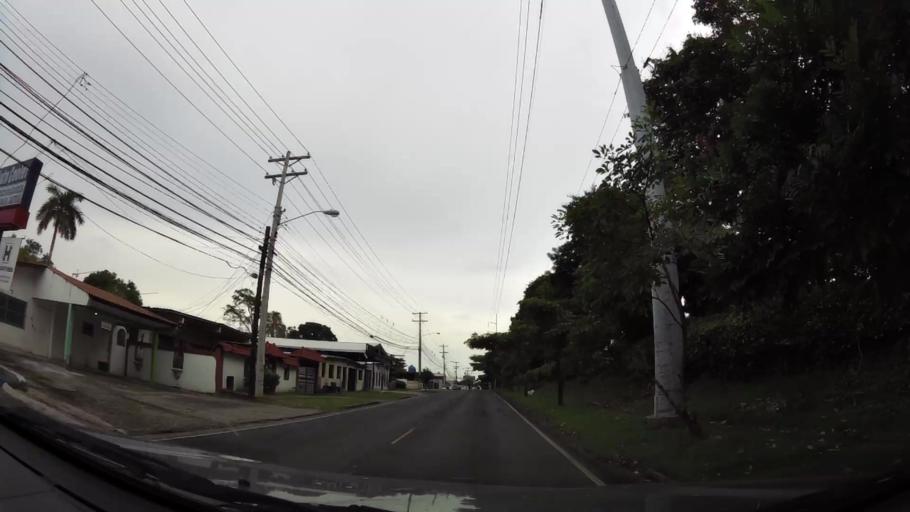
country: PA
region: Panama
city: Panama
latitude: 9.0100
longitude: -79.4963
